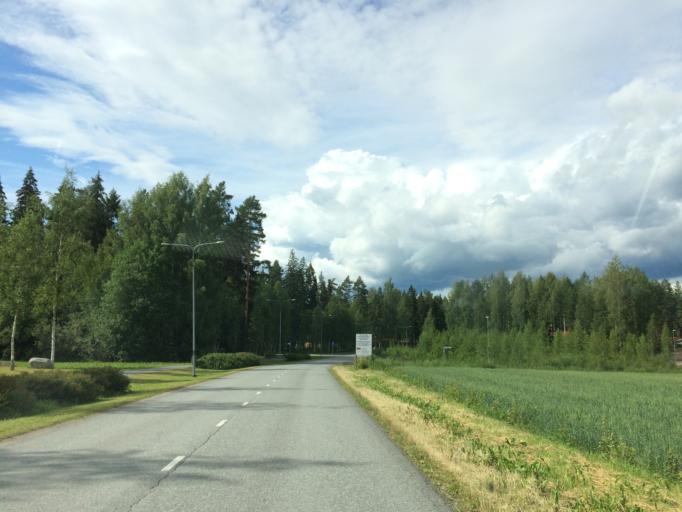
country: FI
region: Haeme
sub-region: Haemeenlinna
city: Turenki
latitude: 60.9317
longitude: 24.6514
